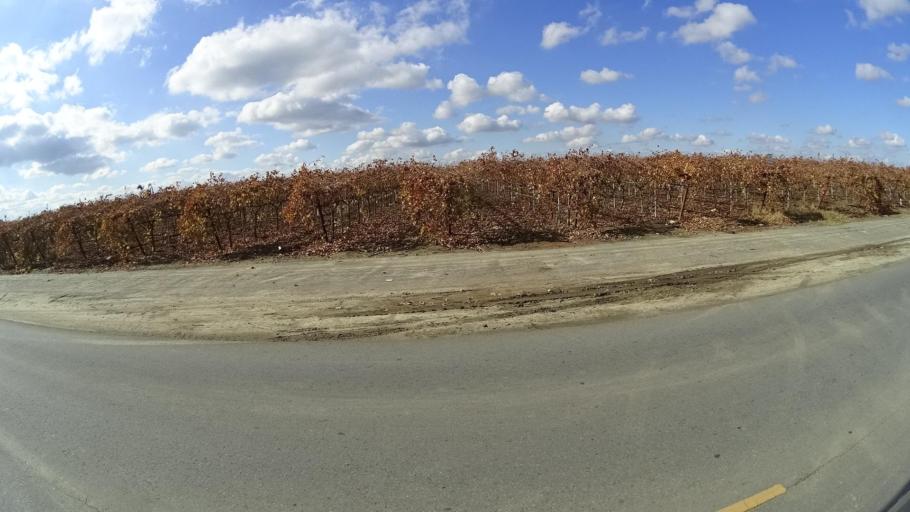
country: US
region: California
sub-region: Kern County
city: McFarland
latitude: 35.6786
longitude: -119.2409
